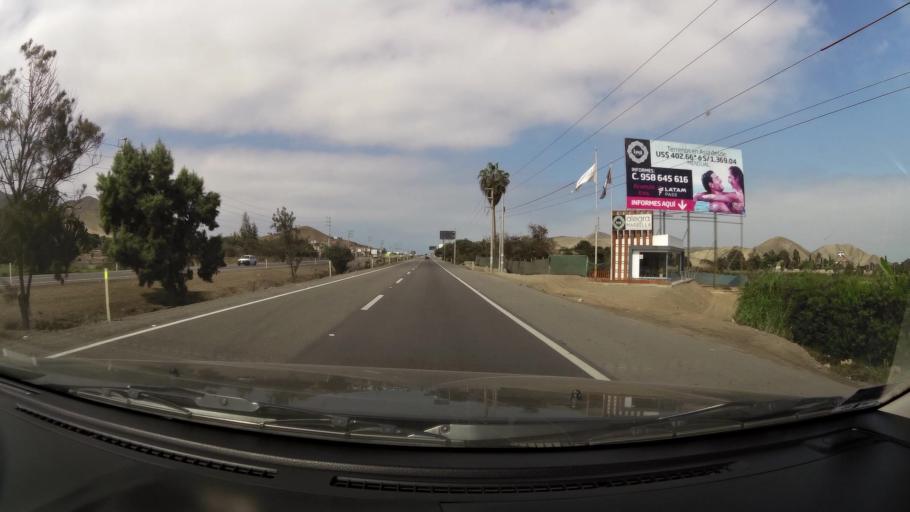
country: PE
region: Lima
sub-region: Provincia de Canete
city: Mala
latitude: -12.7294
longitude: -76.6161
